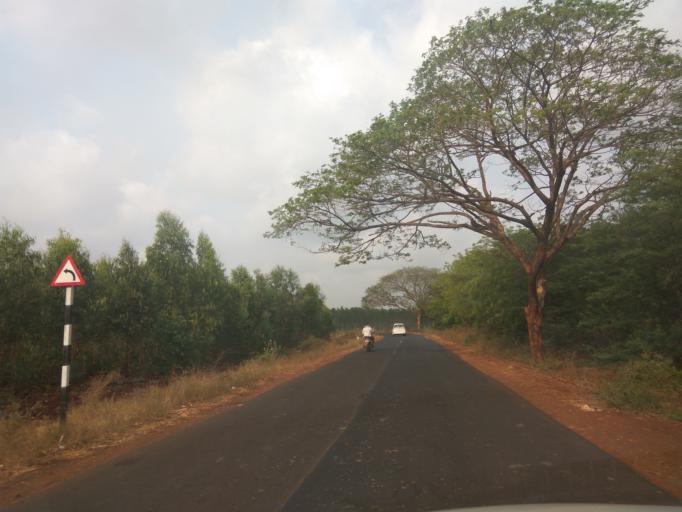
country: IN
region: Andhra Pradesh
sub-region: Prakasam
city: Kandukur
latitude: 15.1987
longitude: 79.8452
